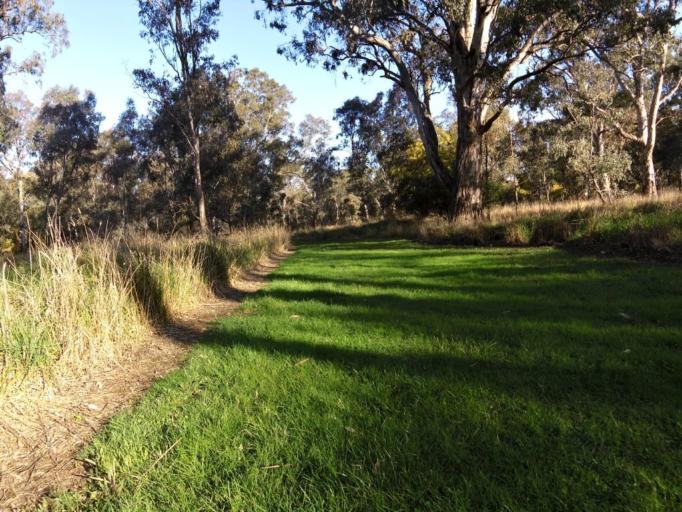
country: AU
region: Victoria
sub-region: Murrindindi
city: Alexandra
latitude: -37.2058
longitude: 145.4265
